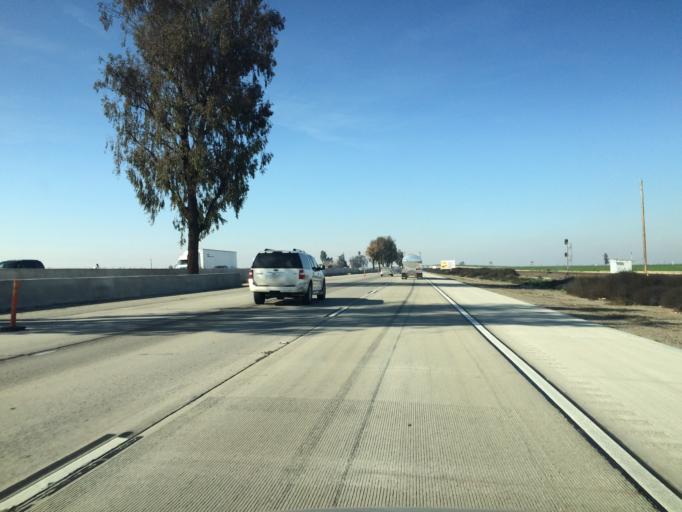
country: US
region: California
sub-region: Tulare County
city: Goshen
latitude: 36.3735
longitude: -119.4359
